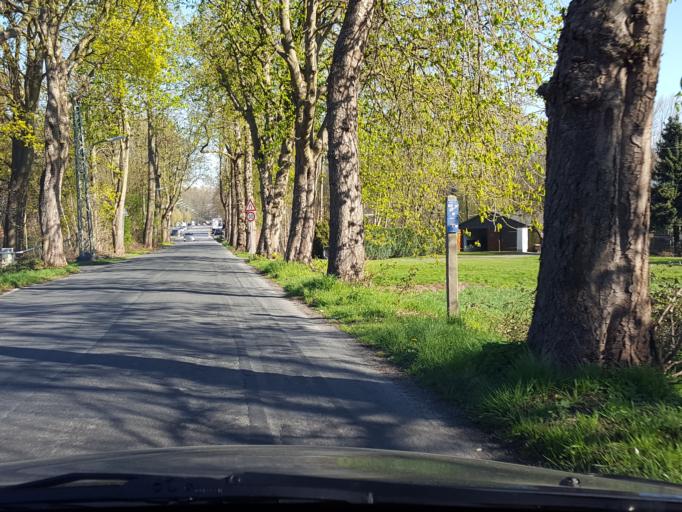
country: DE
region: North Rhine-Westphalia
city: Oer-Erkenschwick
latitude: 51.6442
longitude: 7.2911
